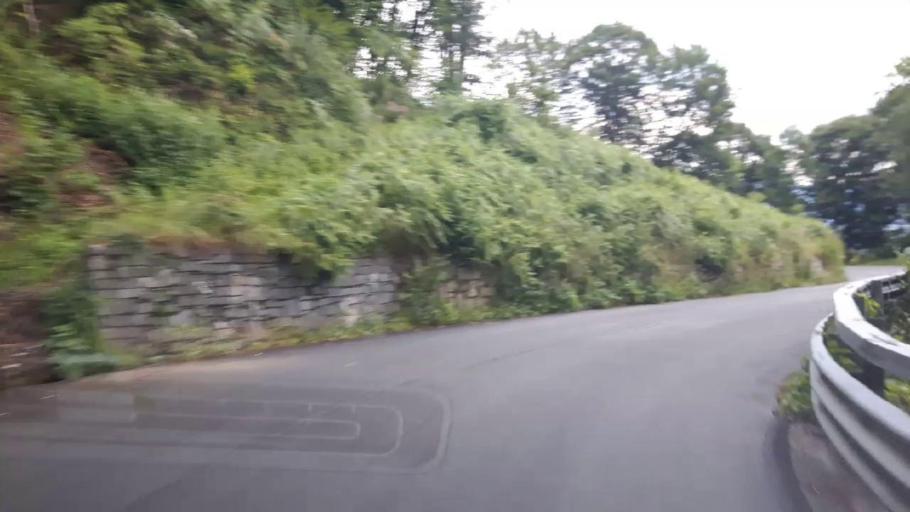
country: IT
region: Piedmont
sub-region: Provincia Verbano-Cusio-Ossola
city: Gignese
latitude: 45.8772
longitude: 8.5109
